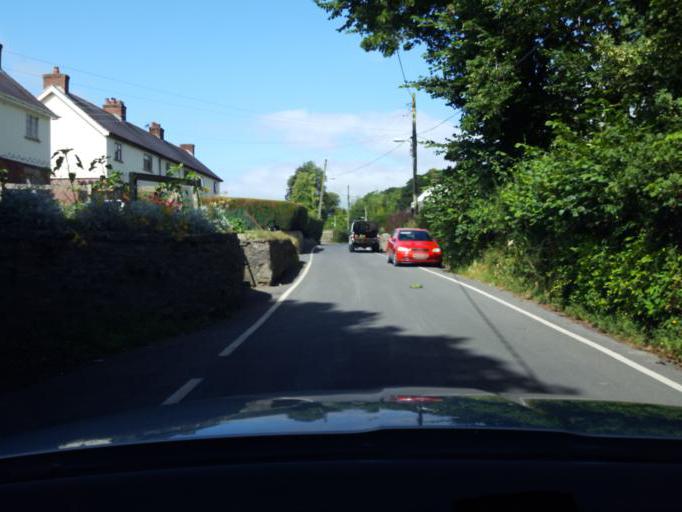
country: GB
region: Wales
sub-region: Denbighshire
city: Corwen
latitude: 52.9823
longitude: -3.3293
